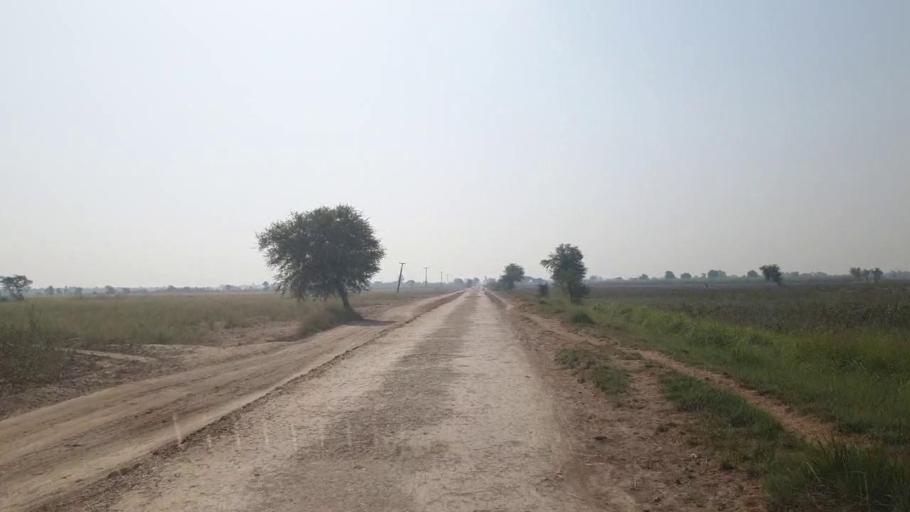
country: PK
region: Sindh
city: Shahdadpur
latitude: 25.9204
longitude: 68.7366
